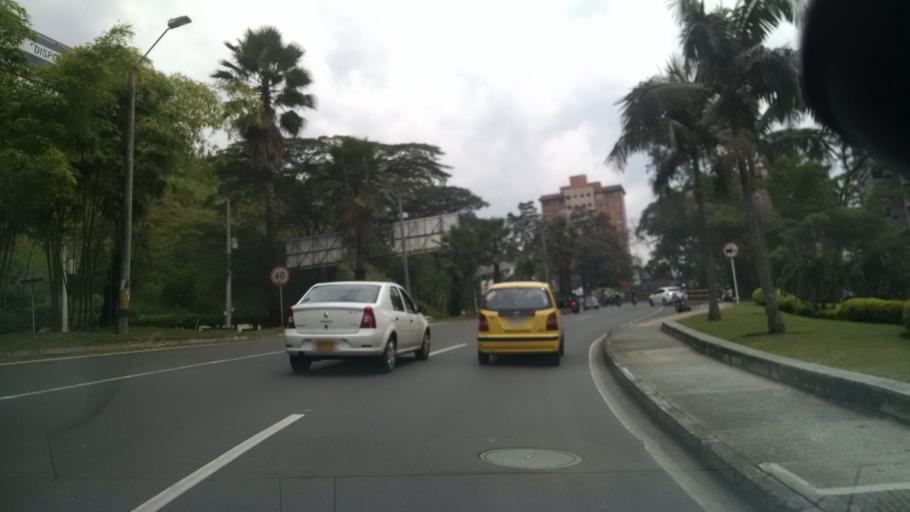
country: CO
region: Antioquia
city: Medellin
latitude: 6.2177
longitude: -75.5645
